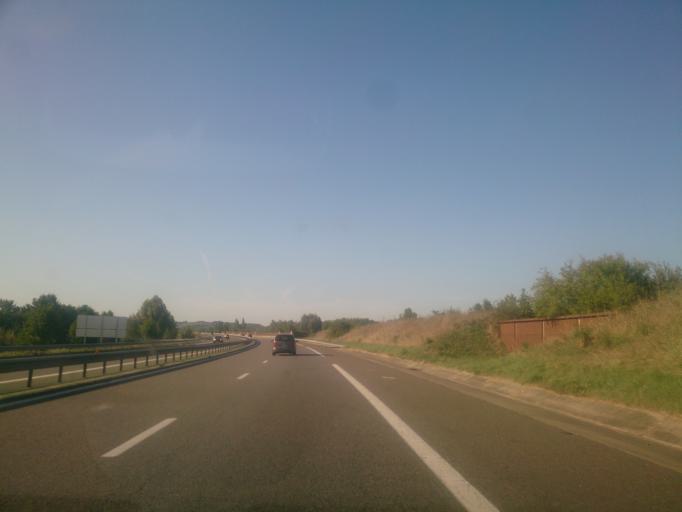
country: FR
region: Midi-Pyrenees
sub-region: Departement du Tarn-et-Garonne
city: Albias
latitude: 44.0657
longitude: 1.4232
